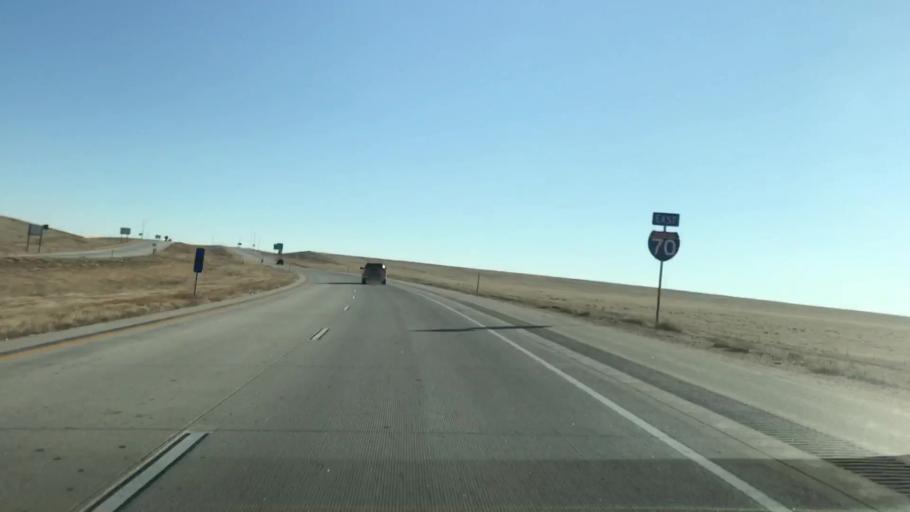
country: US
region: Colorado
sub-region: Lincoln County
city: Limon
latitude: 39.2607
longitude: -103.6583
